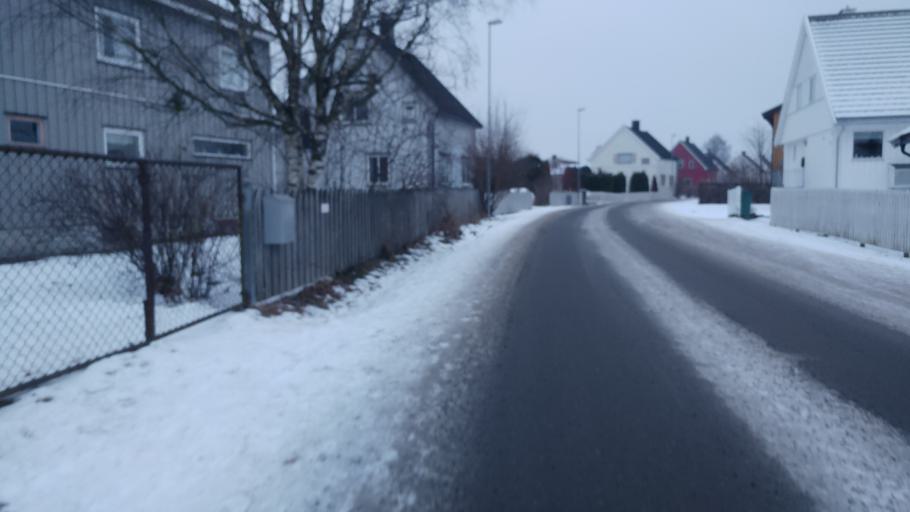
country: NO
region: Akershus
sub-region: Skedsmo
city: Lillestrom
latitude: 59.9627
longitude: 11.0354
